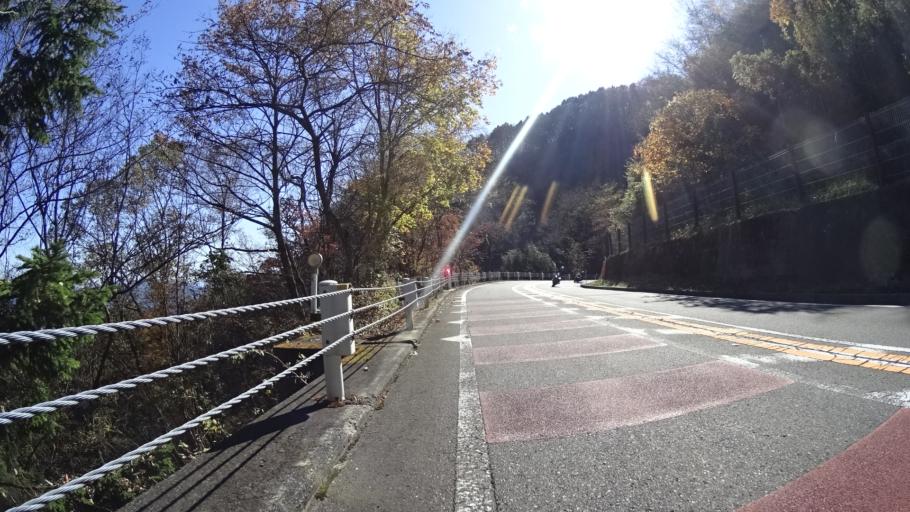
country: JP
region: Yamanashi
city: Uenohara
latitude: 35.7452
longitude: 139.0423
